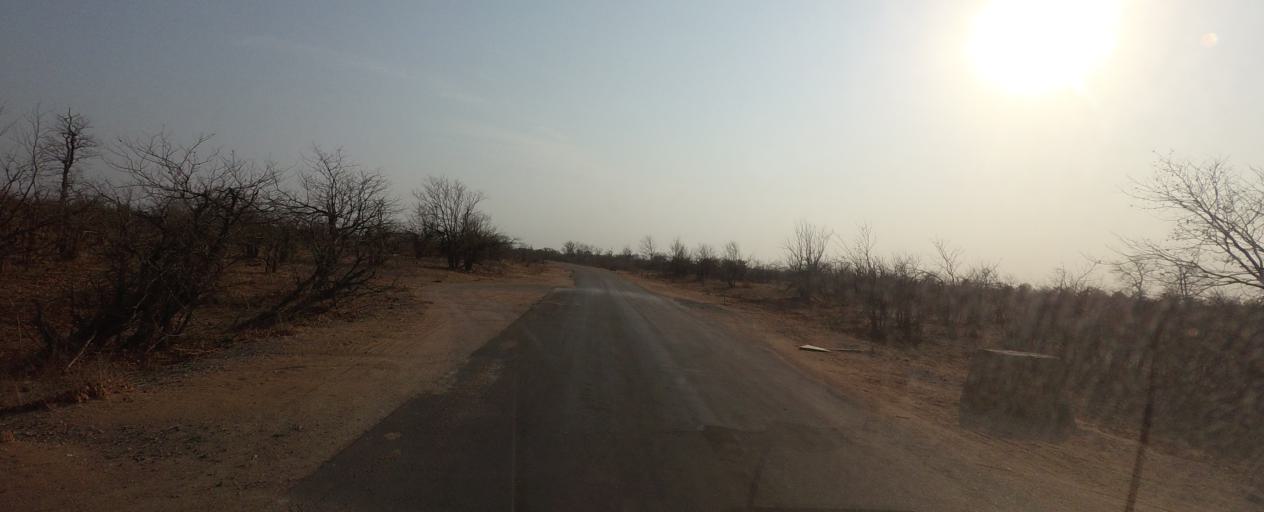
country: ZA
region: Limpopo
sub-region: Mopani District Municipality
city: Giyani
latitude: -23.0928
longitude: 31.4195
